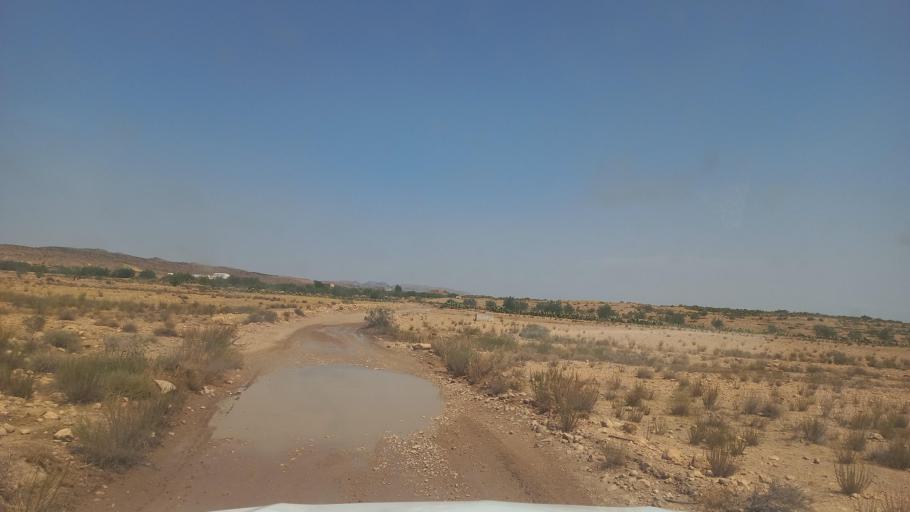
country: TN
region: Al Qasrayn
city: Kasserine
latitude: 35.2908
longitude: 8.9529
